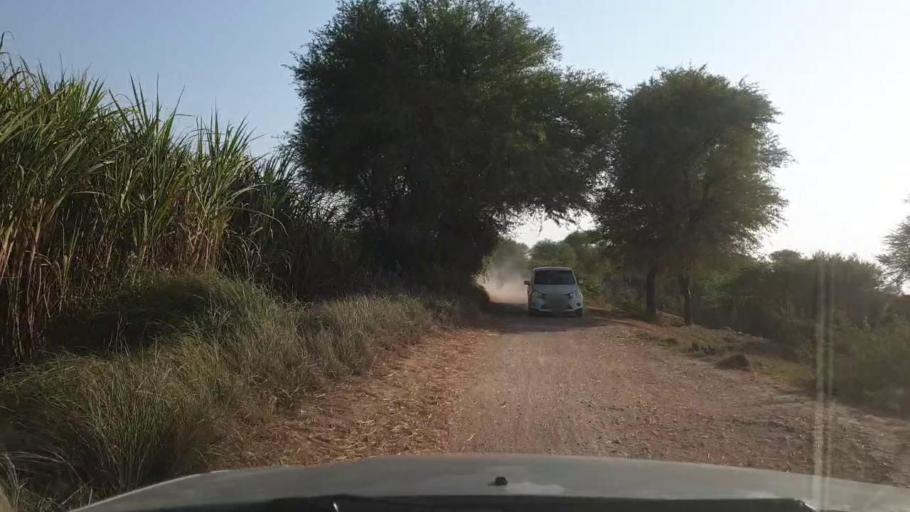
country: PK
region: Sindh
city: Tando Muhammad Khan
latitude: 25.0630
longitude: 68.5072
